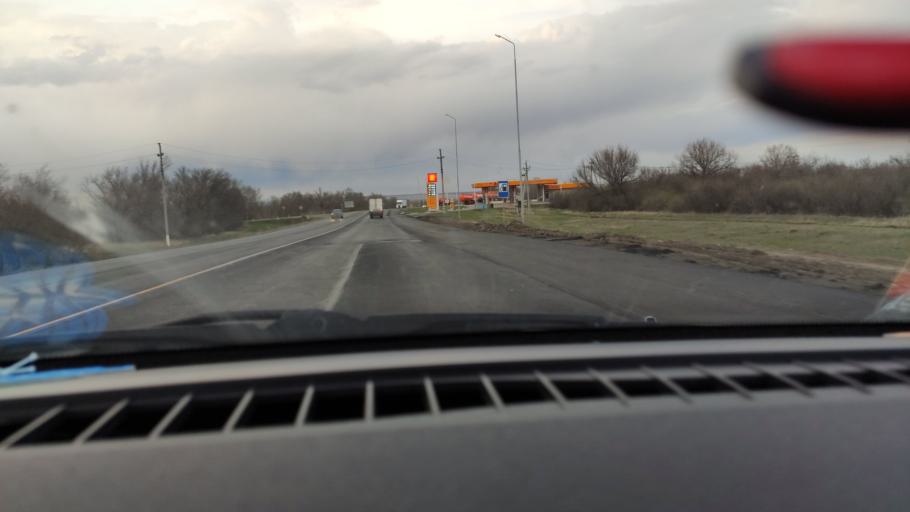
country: RU
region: Saratov
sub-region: Saratovskiy Rayon
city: Saratov
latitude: 51.6847
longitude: 46.0029
